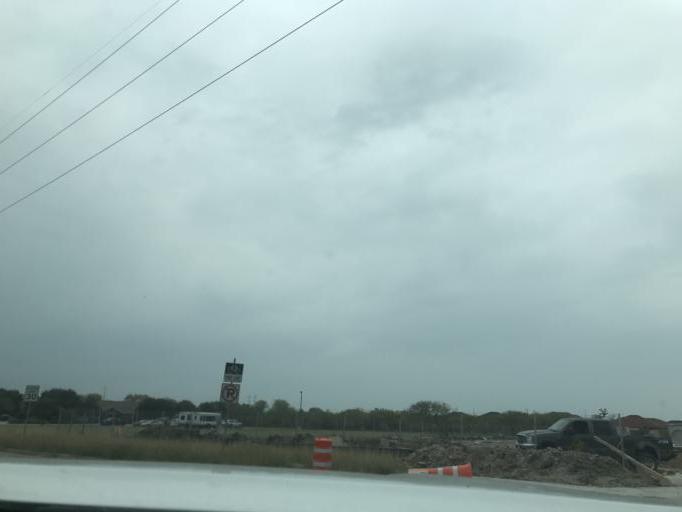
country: US
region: Texas
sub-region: Nueces County
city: Corpus Christi
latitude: 27.6757
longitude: -97.3475
